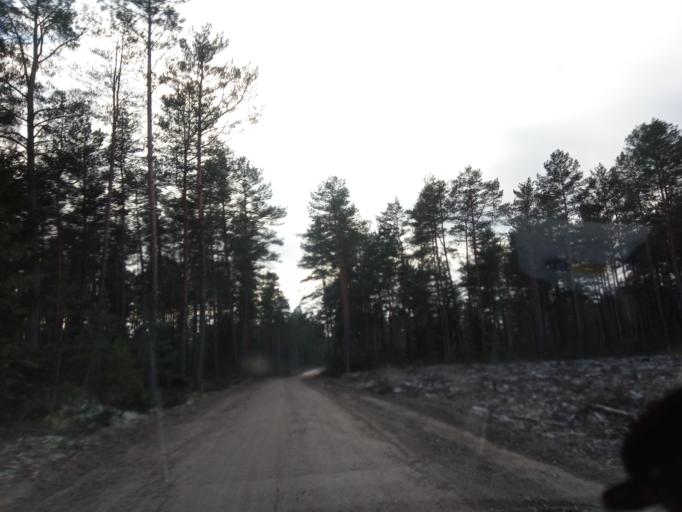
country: LT
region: Alytaus apskritis
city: Varena
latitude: 53.9777
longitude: 24.3305
